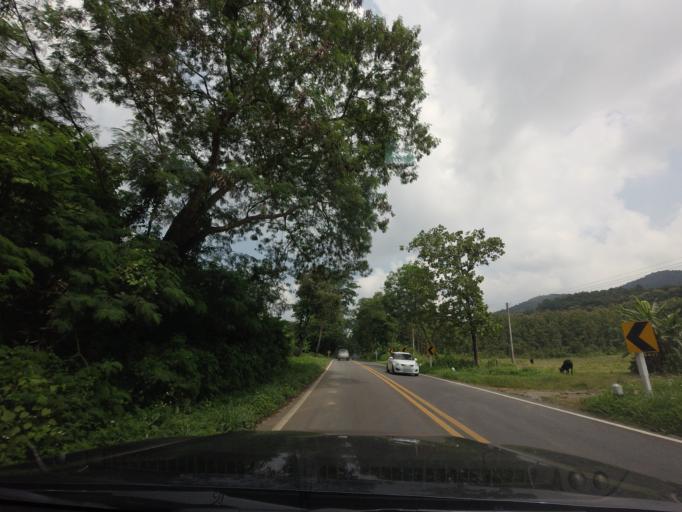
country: TH
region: Nan
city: Pua
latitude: 19.1229
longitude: 100.9514
